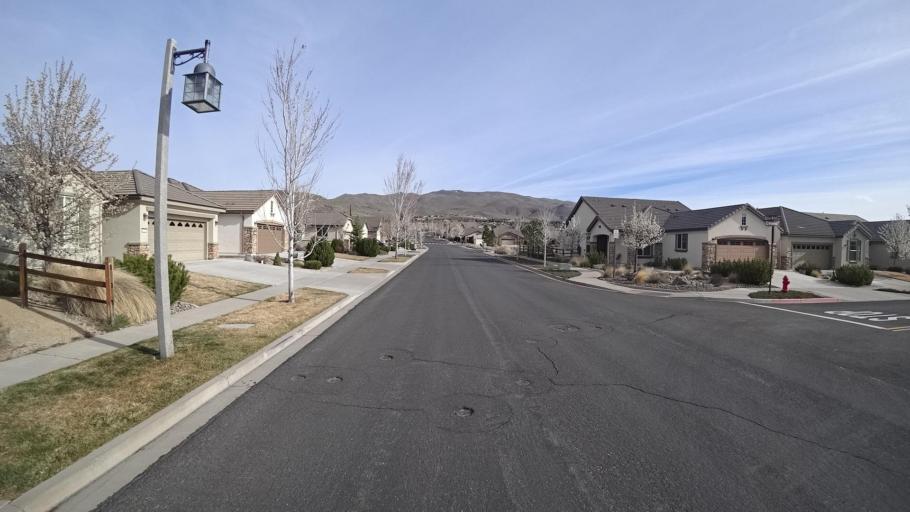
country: US
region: Nevada
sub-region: Washoe County
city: Mogul
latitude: 39.5234
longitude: -119.9539
